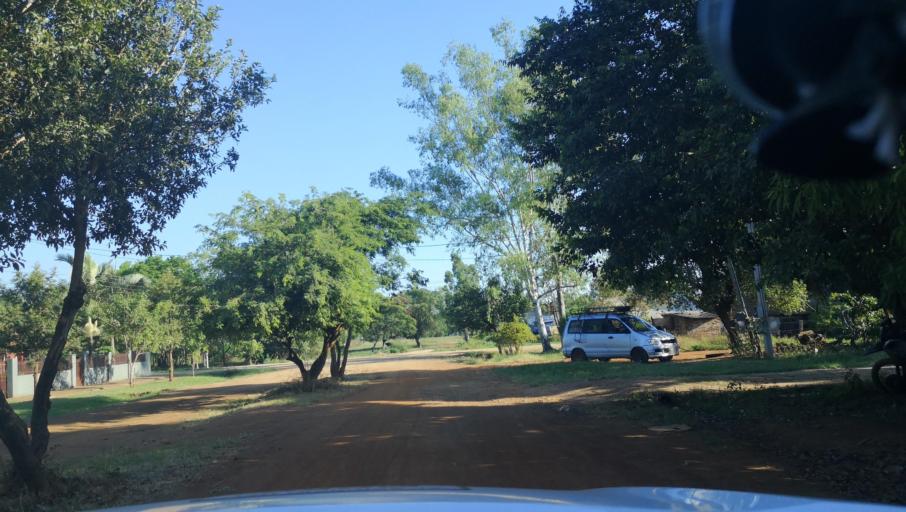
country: PY
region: Itapua
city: Carmen del Parana
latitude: -27.1546
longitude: -56.2427
